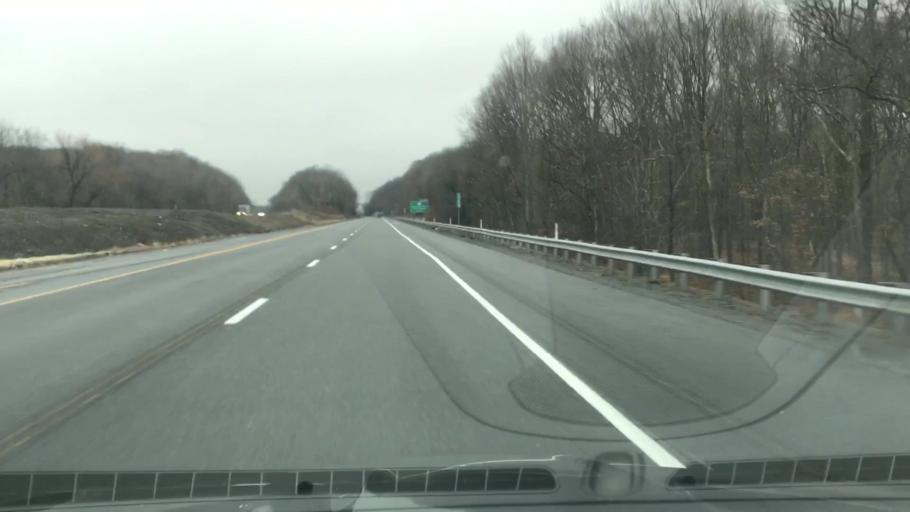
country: US
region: Pennsylvania
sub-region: Pike County
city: Hemlock Farms
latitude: 41.3497
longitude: -75.0101
